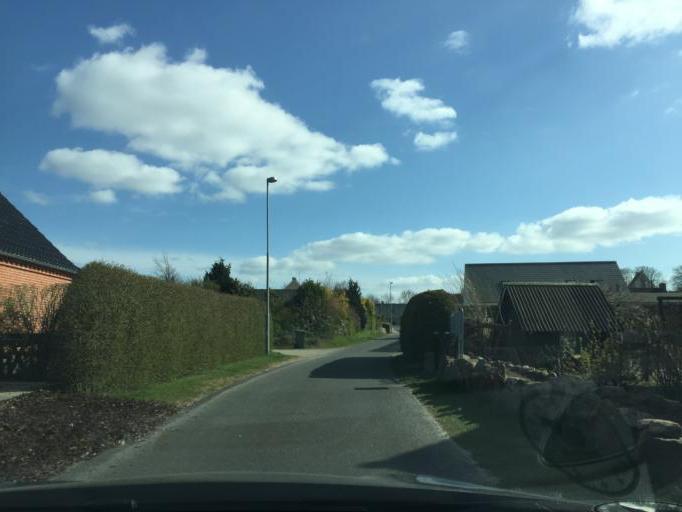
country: DK
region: South Denmark
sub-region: Faaborg-Midtfyn Kommune
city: Arslev
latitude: 55.3107
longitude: 10.4927
